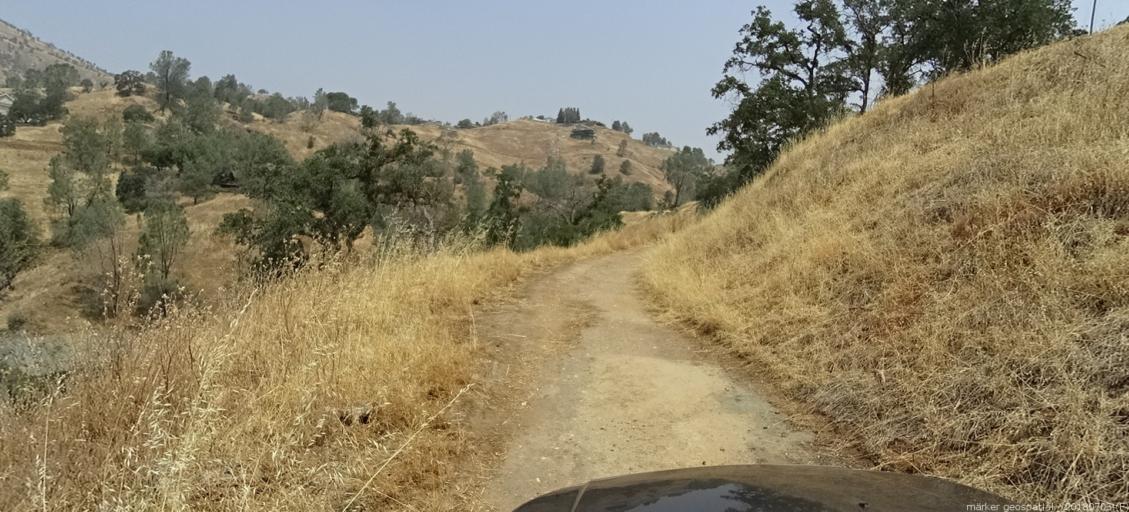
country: US
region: California
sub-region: Fresno County
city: Auberry
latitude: 37.0470
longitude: -119.6510
